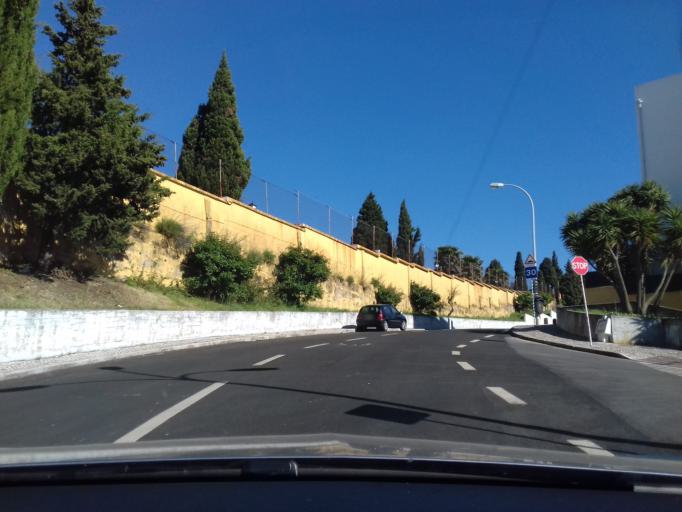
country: PT
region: Lisbon
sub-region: Oeiras
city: Oeiras
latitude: 38.6994
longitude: -9.3090
